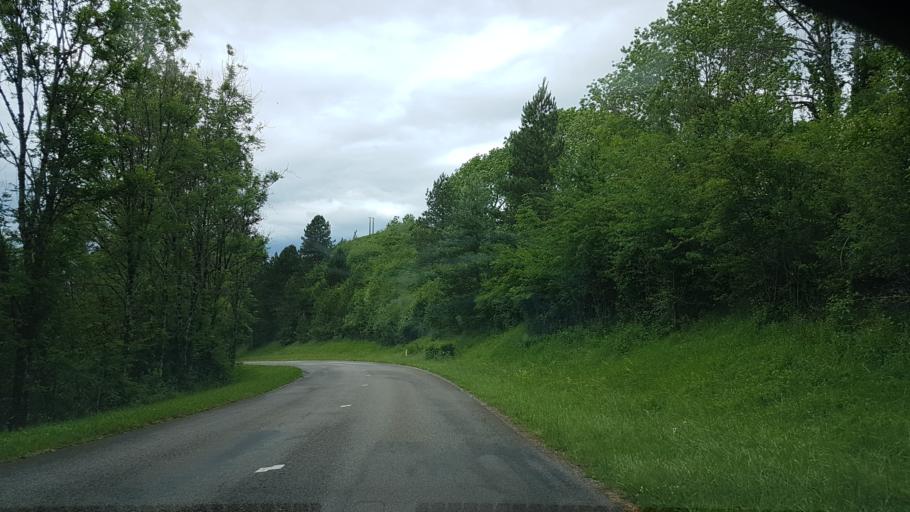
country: FR
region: Franche-Comte
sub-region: Departement du Jura
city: Clairvaux-les-Lacs
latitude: 46.5768
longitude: 5.7380
